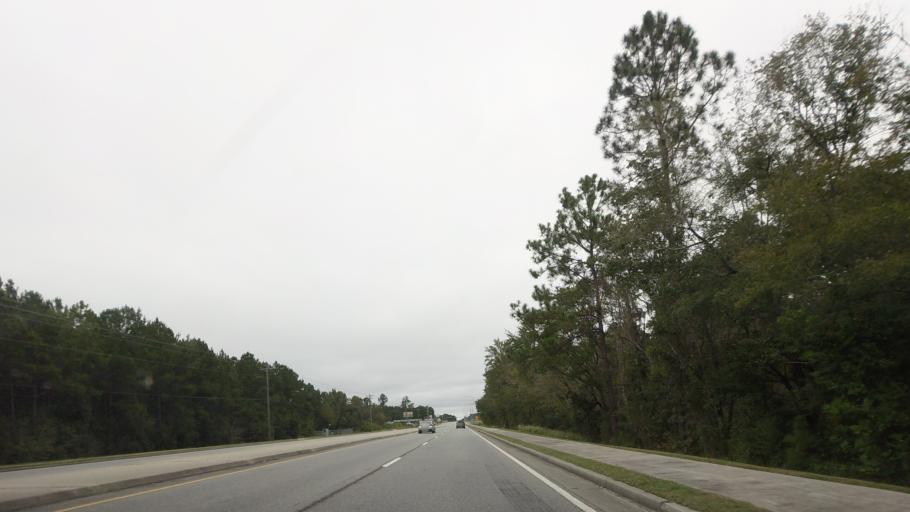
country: US
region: Georgia
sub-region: Berrien County
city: Ray City
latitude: 30.9668
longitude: -83.2178
